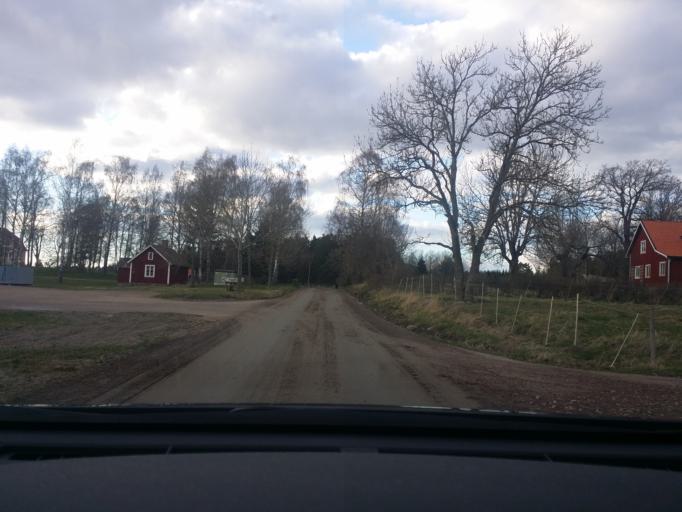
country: SE
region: Vaestmanland
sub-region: Vasteras
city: Vasteras
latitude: 59.5557
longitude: 16.4497
